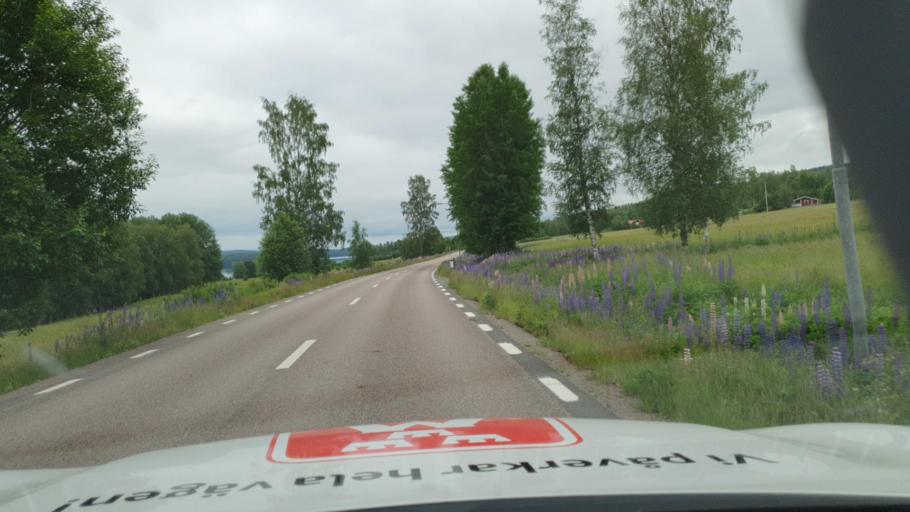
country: SE
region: Vaermland
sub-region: Sunne Kommun
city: Sunne
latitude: 59.8986
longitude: 12.9144
